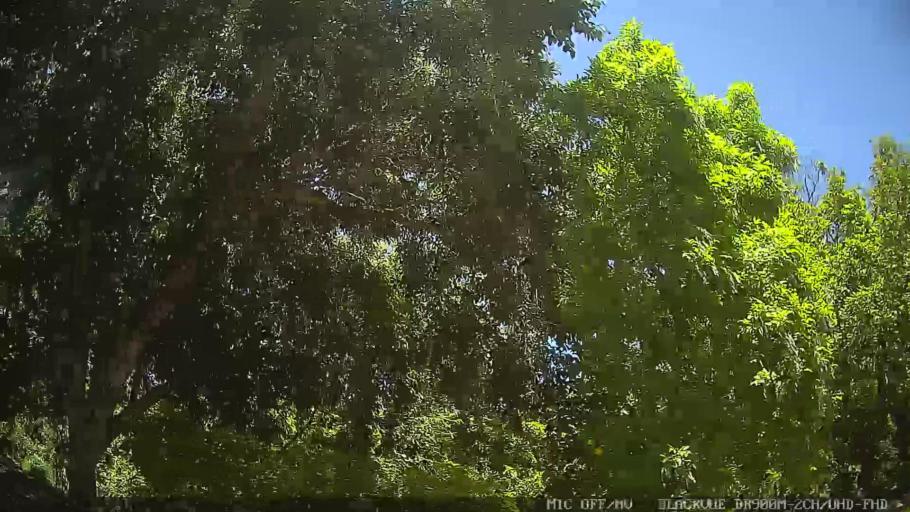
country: BR
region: Sao Paulo
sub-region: Pedreira
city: Pedreira
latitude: -22.7529
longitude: -46.9156
